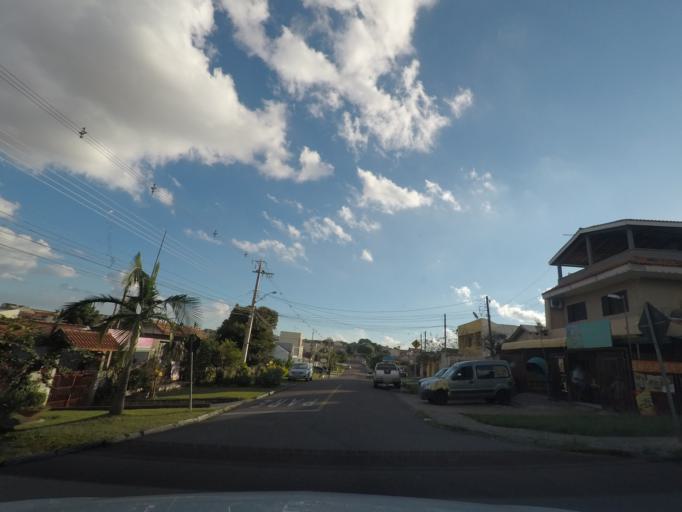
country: BR
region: Parana
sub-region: Sao Jose Dos Pinhais
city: Sao Jose dos Pinhais
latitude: -25.4969
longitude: -49.2597
